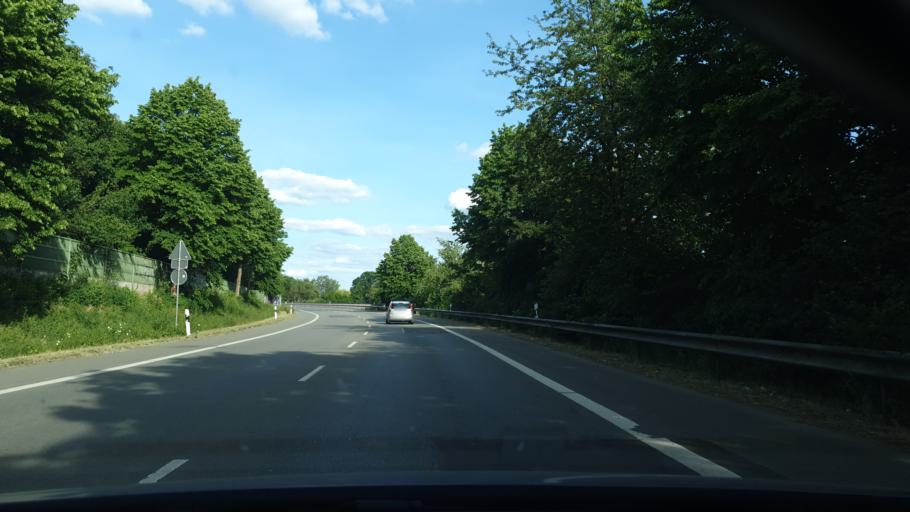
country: DE
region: North Rhine-Westphalia
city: Buende
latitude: 52.1950
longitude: 8.5718
